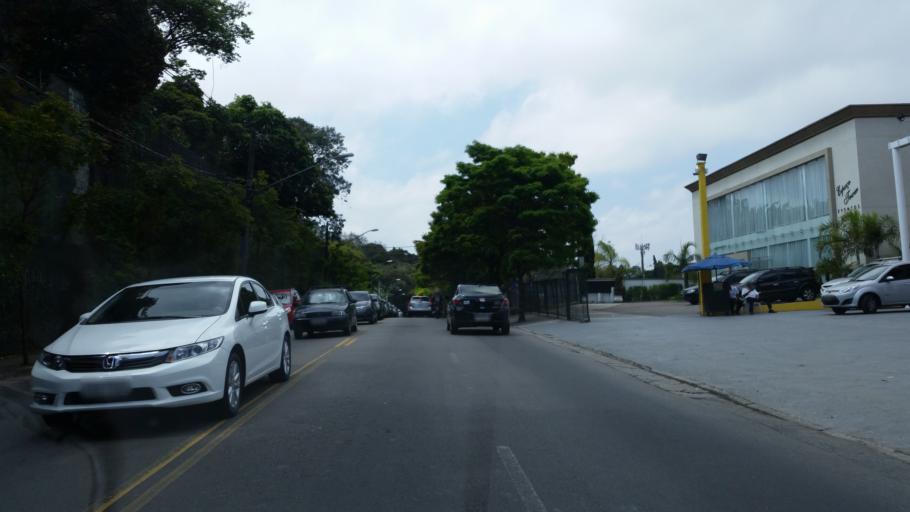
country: BR
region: Sao Paulo
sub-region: Diadema
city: Diadema
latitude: -23.6525
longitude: -46.6879
